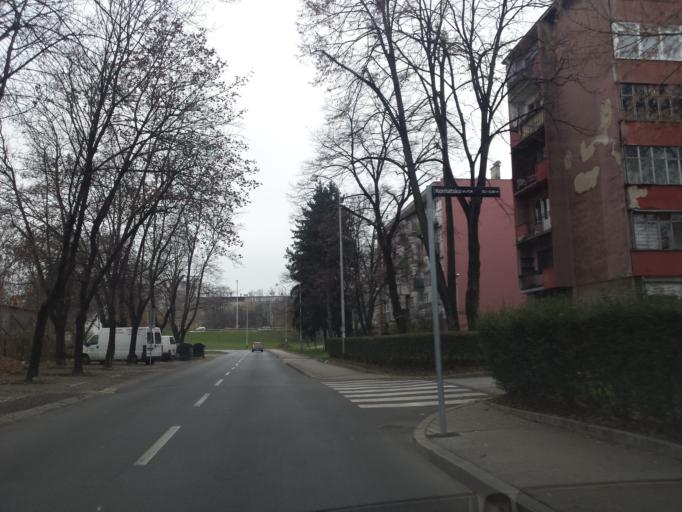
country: HR
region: Grad Zagreb
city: Novi Zagreb
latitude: 45.7975
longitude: 16.0043
